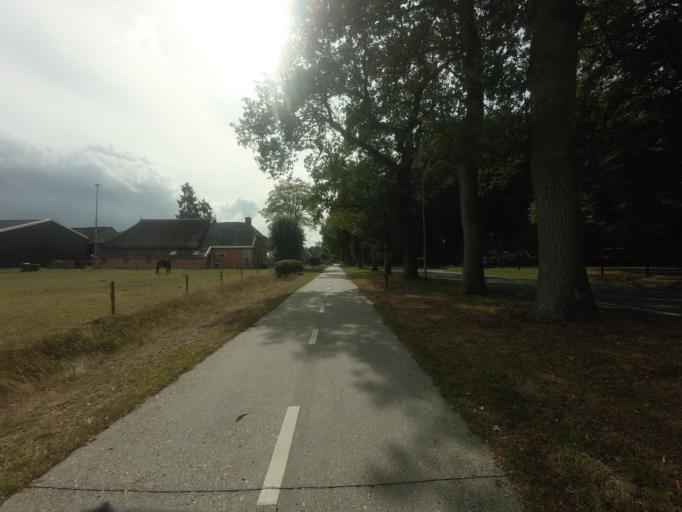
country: NL
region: Drenthe
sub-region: Gemeente Assen
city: Assen
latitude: 53.0493
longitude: 6.4565
